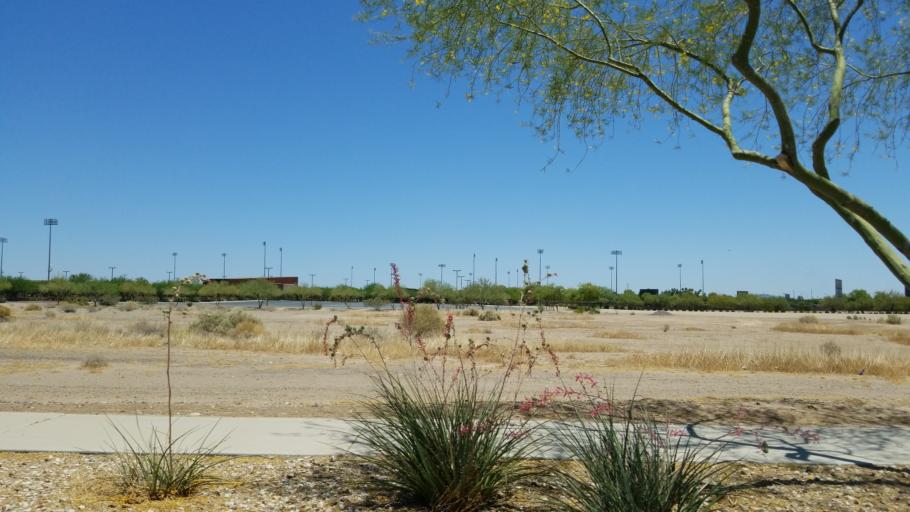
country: US
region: Arizona
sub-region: Maricopa County
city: Litchfield Park
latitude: 33.5118
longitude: -112.3000
